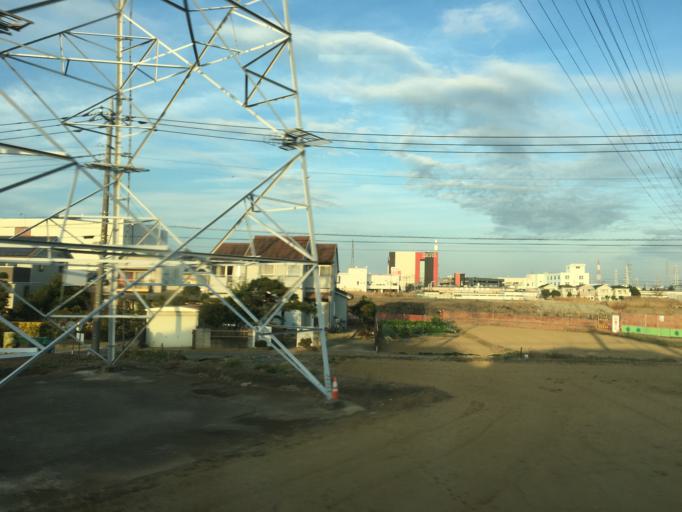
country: JP
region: Saitama
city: Konosu
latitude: 36.0776
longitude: 139.4871
